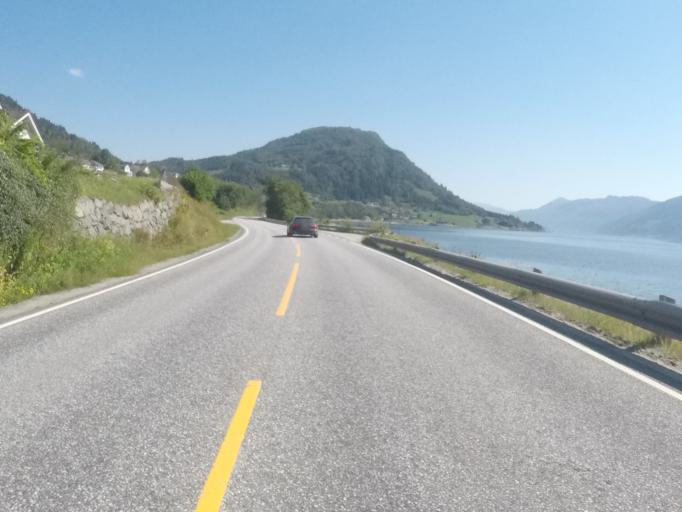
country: NO
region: Sogn og Fjordane
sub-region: Eid
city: Nordfjordeid
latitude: 61.9183
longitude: 5.7787
